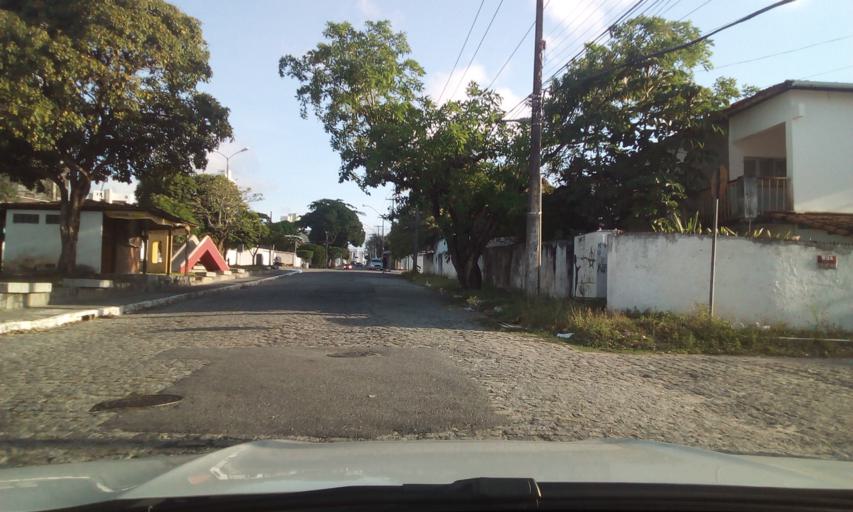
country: BR
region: Paraiba
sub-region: Joao Pessoa
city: Joao Pessoa
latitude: -7.1039
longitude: -34.8559
